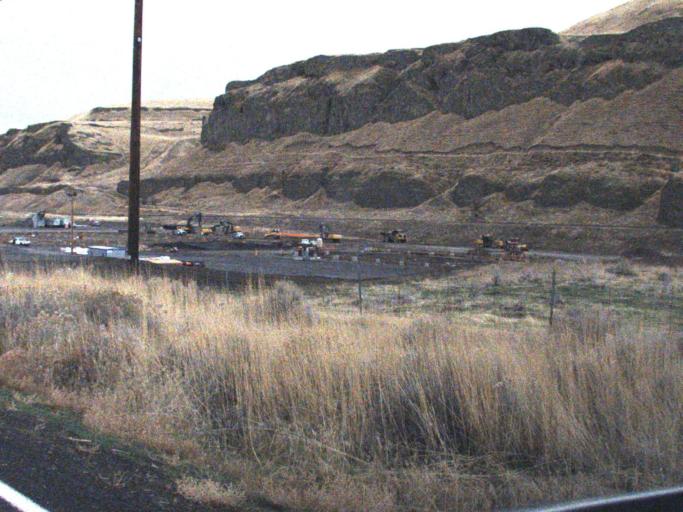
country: US
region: Washington
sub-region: Walla Walla County
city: Waitsburg
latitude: 46.5685
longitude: -118.1944
